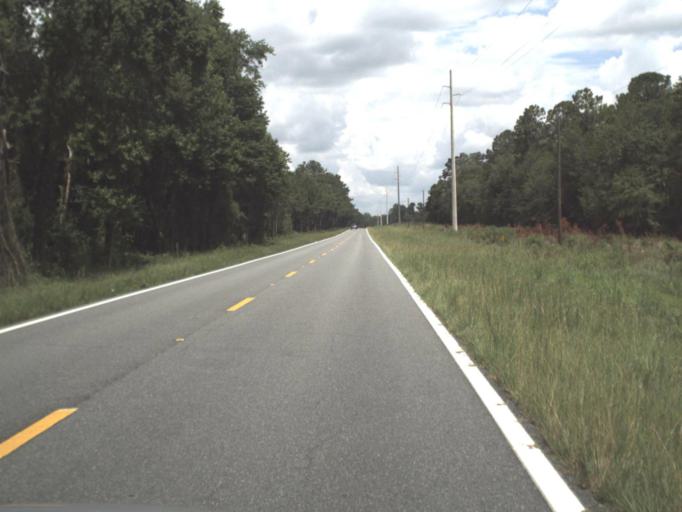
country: US
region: Florida
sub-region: Union County
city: Lake Butler
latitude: 29.9052
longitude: -82.3664
